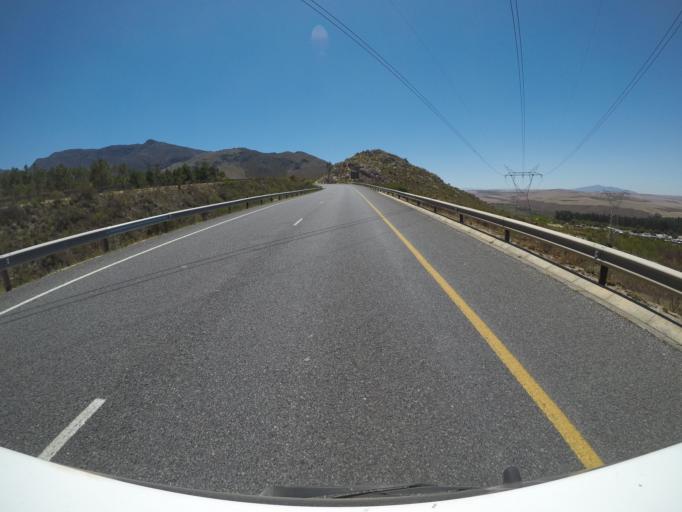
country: ZA
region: Western Cape
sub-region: Overberg District Municipality
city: Grabouw
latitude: -34.2209
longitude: 19.1886
